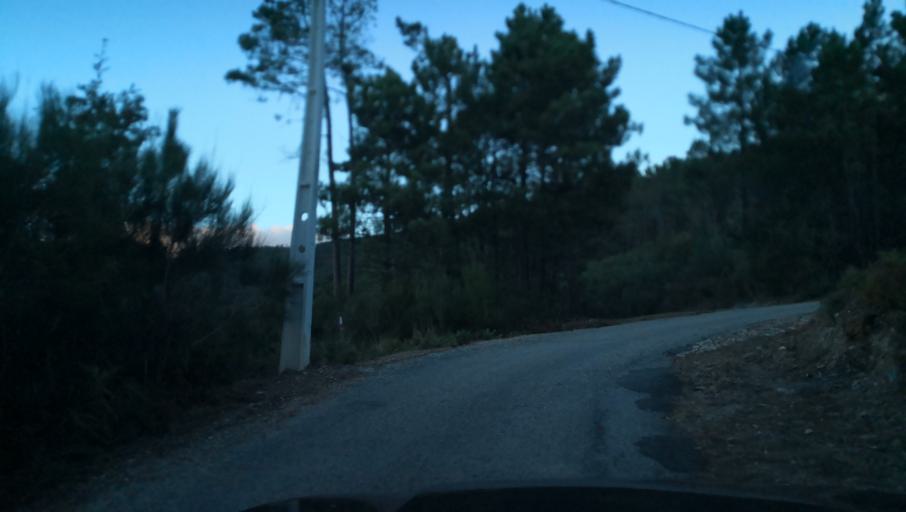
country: PT
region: Vila Real
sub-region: Santa Marta de Penaguiao
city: Santa Marta de Penaguiao
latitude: 41.2608
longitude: -7.8296
